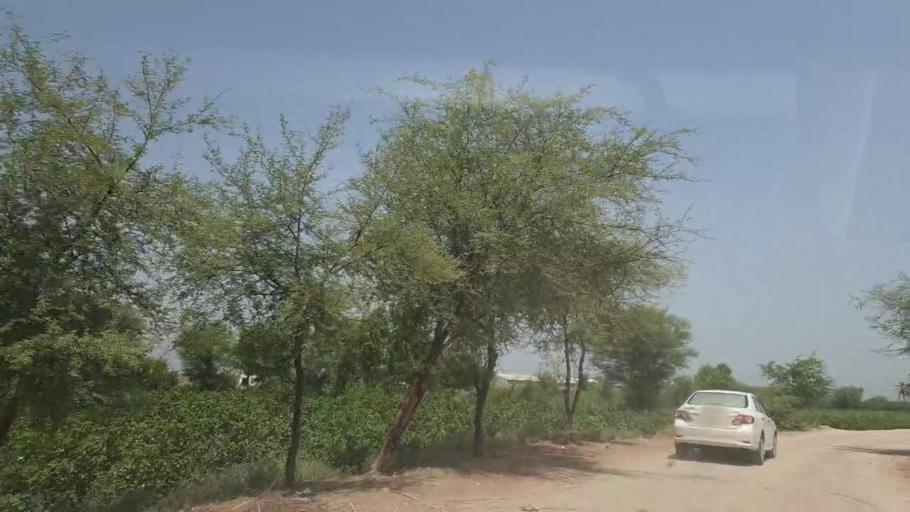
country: PK
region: Sindh
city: Gambat
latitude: 27.2993
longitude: 68.6077
